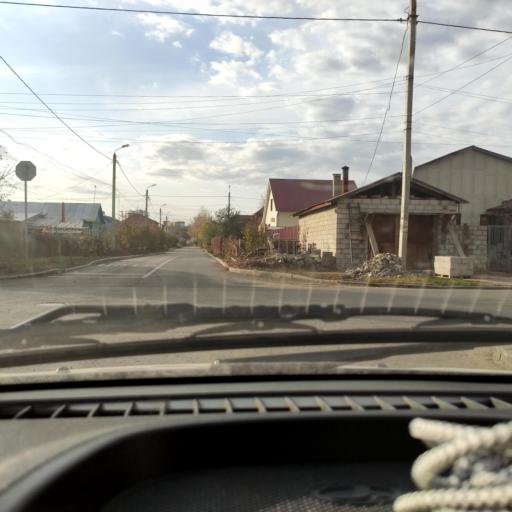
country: RU
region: Samara
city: Tol'yatti
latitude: 53.5277
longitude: 49.4172
